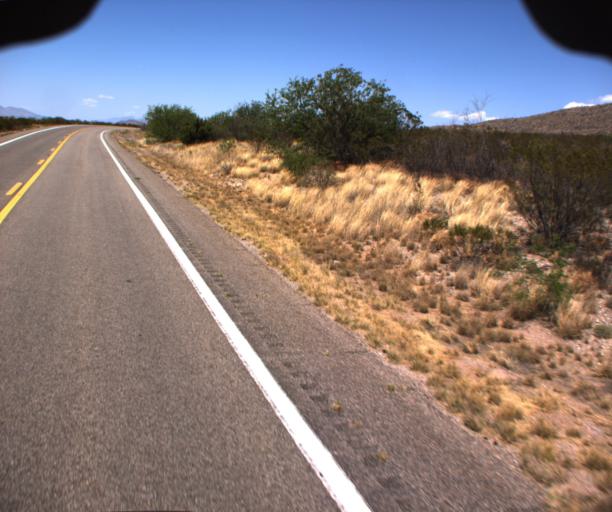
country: US
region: Arizona
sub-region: Cochise County
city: Tombstone
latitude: 31.5855
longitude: -110.0386
